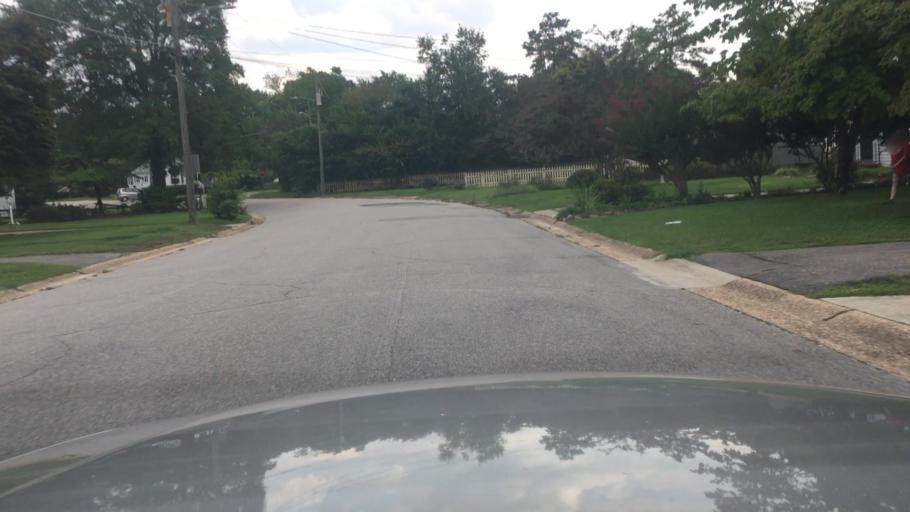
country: US
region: North Carolina
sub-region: Cumberland County
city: Fayetteville
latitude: 35.0719
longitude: -78.9165
